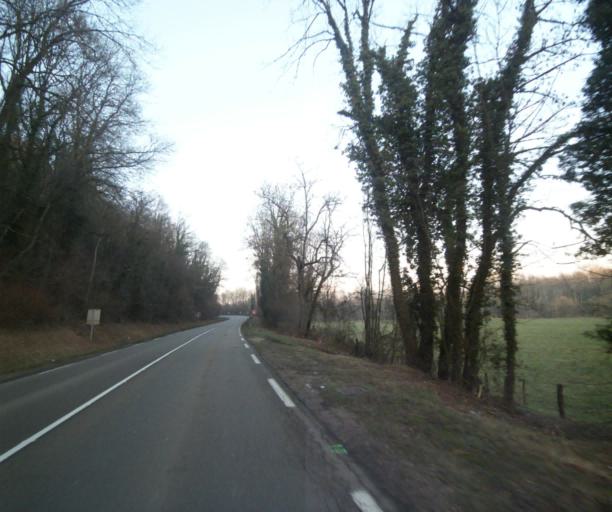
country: FR
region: Champagne-Ardenne
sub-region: Departement de la Haute-Marne
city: Bienville
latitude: 48.5982
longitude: 5.0321
